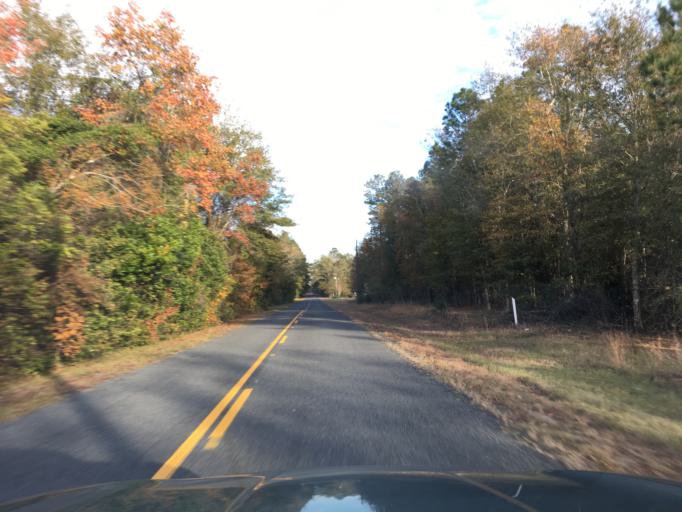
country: US
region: South Carolina
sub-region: Lexington County
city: Leesville
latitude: 33.6845
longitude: -81.3770
